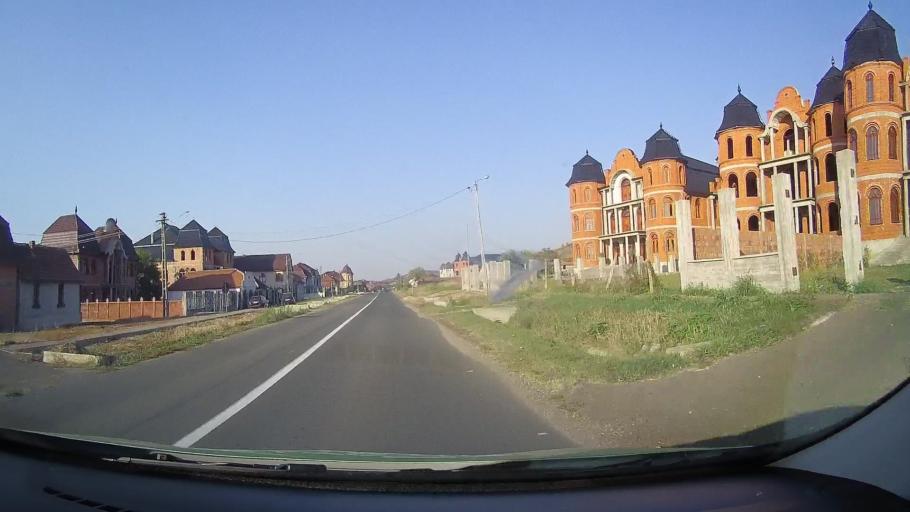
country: RO
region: Arad
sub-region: Comuna Covasint
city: Covasint
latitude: 46.1907
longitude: 21.6051
